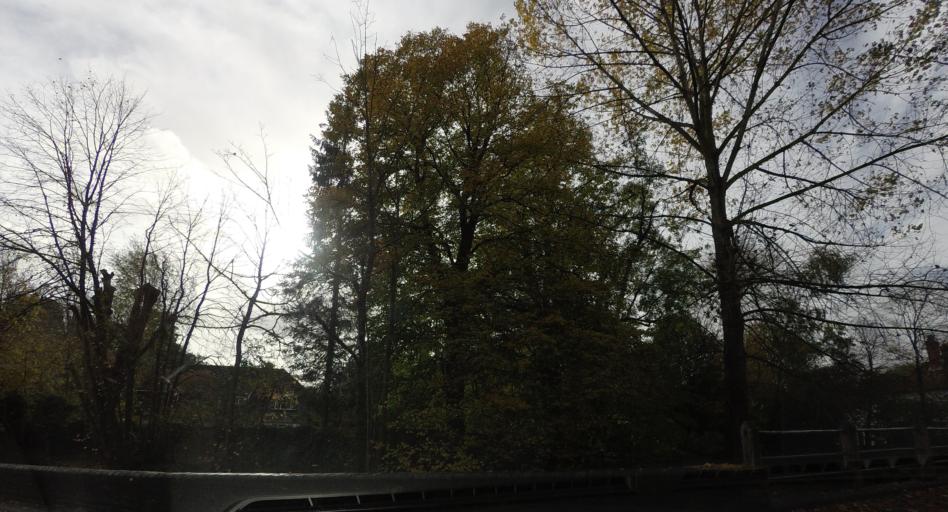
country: GB
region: England
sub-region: Kent
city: Shoreham
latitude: 51.3335
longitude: 0.1814
